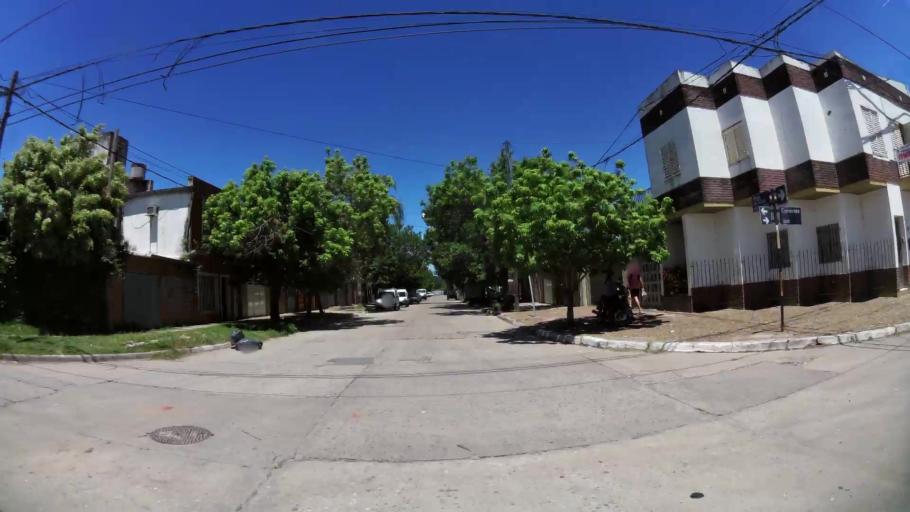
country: AR
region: Santa Fe
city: Santa Fe de la Vera Cruz
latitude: -31.6508
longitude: -60.7258
